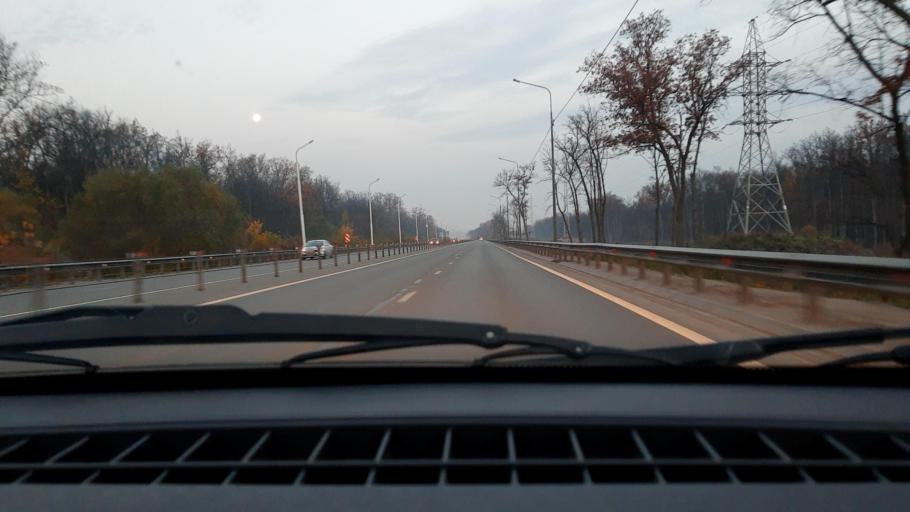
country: RU
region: Bashkortostan
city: Ufa
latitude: 54.6982
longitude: 55.8917
